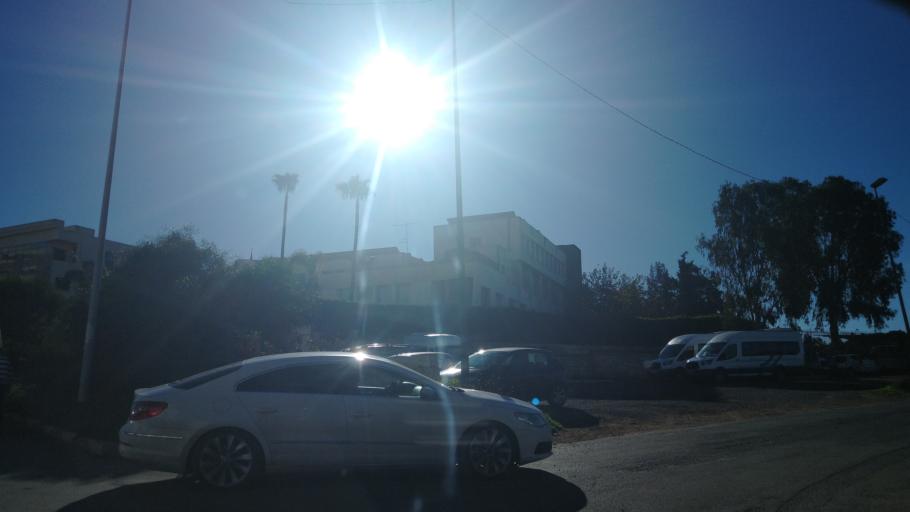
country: MA
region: Rabat-Sale-Zemmour-Zaer
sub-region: Rabat
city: Rabat
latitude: 33.9923
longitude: -6.8586
